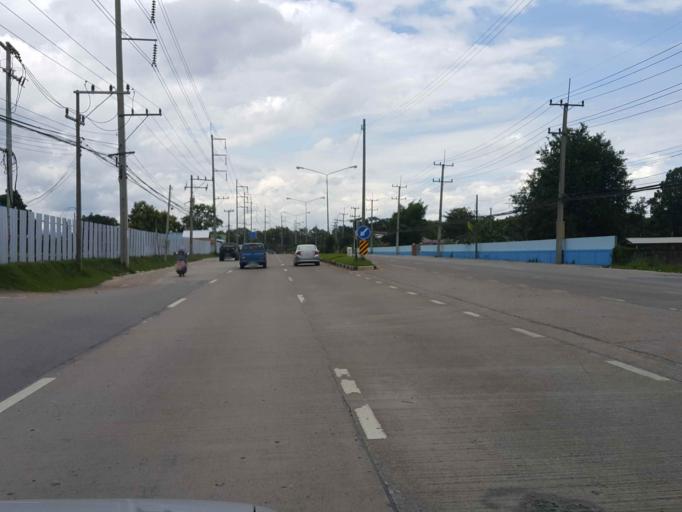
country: TH
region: Chiang Mai
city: San Sai
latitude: 18.8859
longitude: 98.9567
